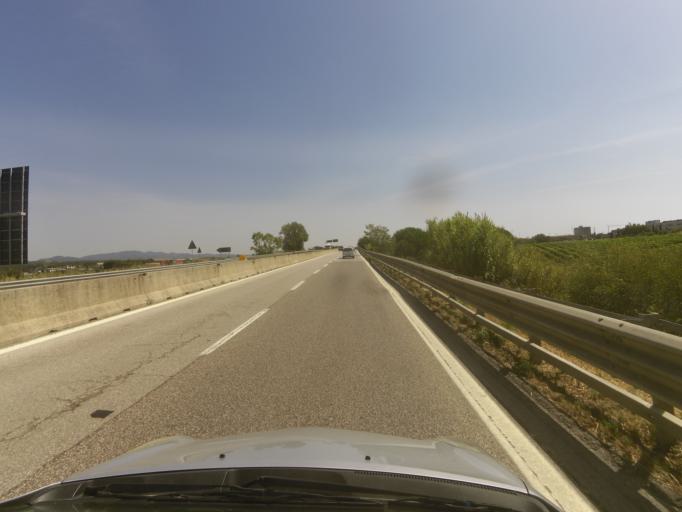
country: IT
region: Tuscany
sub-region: Provincia di Livorno
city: Cecina
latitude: 43.3190
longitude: 10.5332
